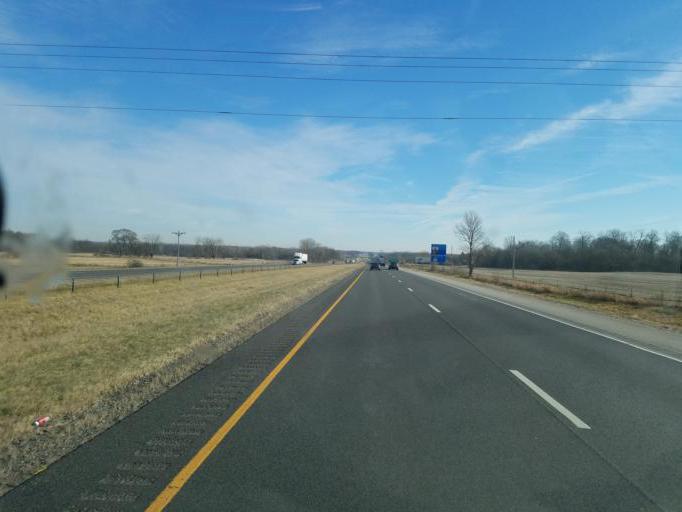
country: US
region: Indiana
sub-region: Wayne County
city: Centerville
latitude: 39.8593
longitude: -85.0151
